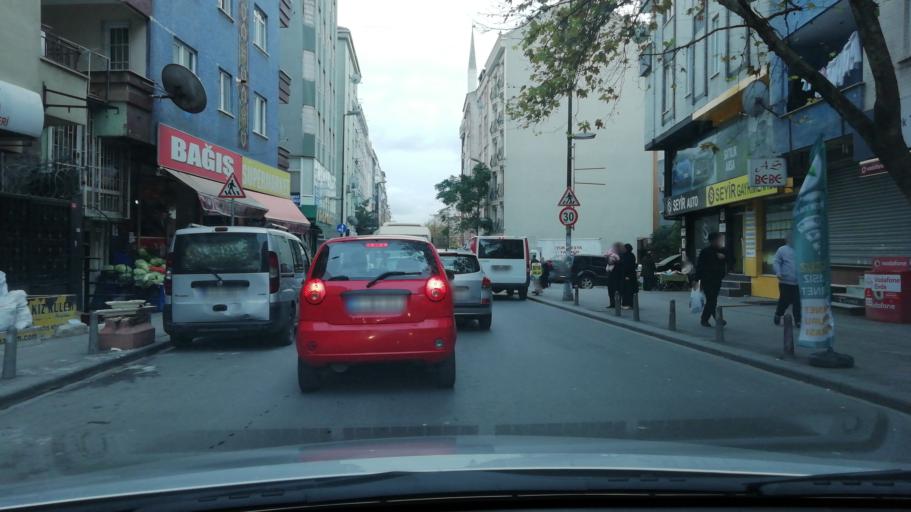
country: TR
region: Istanbul
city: Bahcelievler
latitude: 41.0050
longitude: 28.8387
